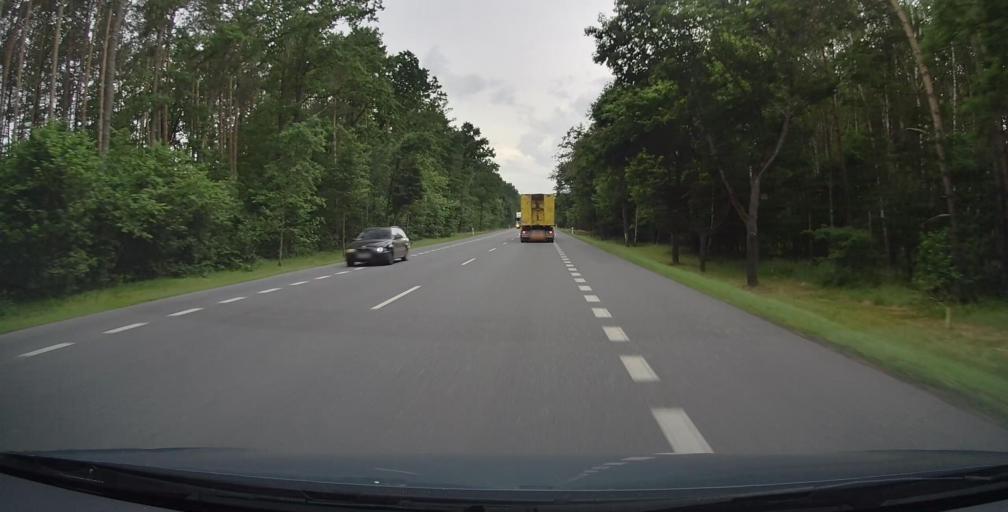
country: PL
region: Lublin Voivodeship
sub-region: Powiat bialski
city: Zalesie
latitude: 52.0363
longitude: 23.4115
